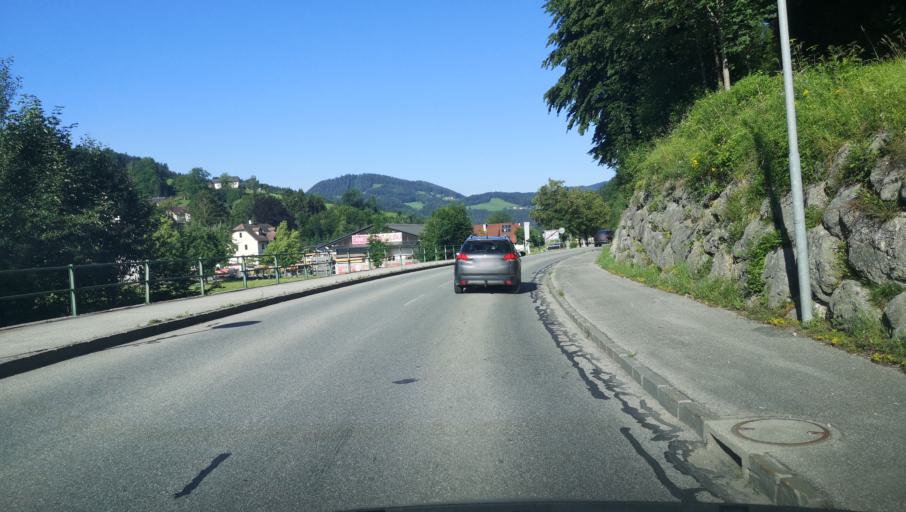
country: AT
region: Lower Austria
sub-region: Politischer Bezirk Amstetten
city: Ybbsitz
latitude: 47.9468
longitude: 14.8855
